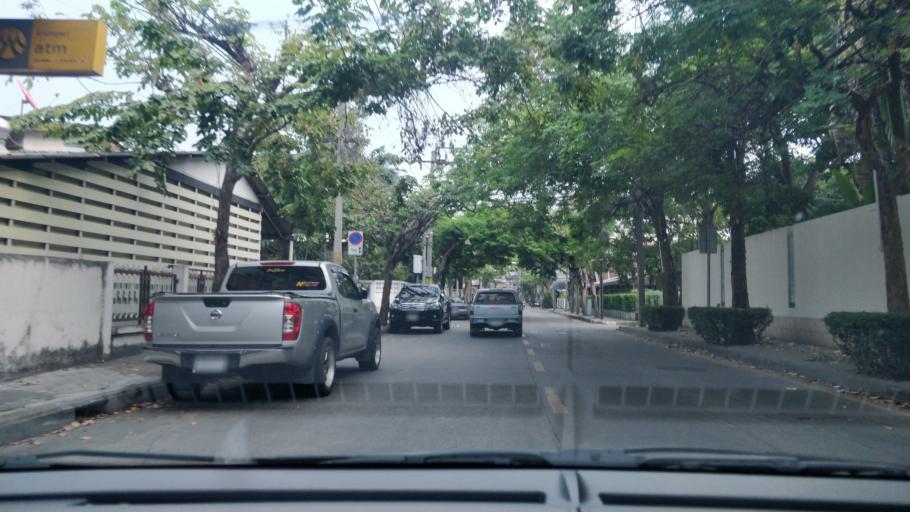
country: TH
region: Bangkok
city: Suan Luang
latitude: 13.7437
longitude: 100.6320
